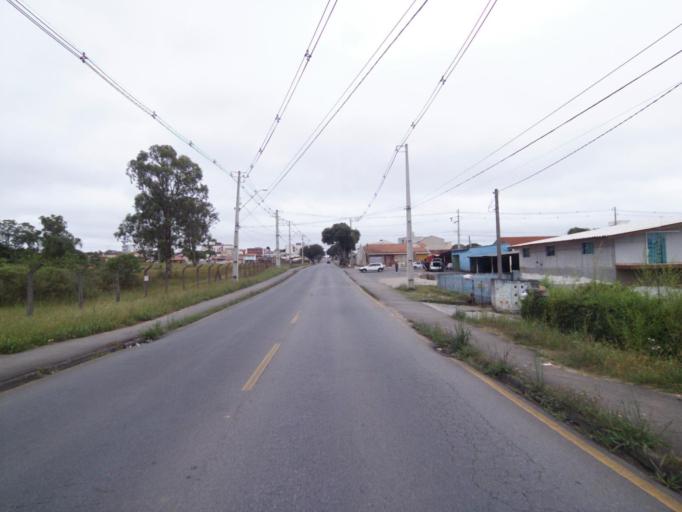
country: BR
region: Parana
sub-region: Sao Jose Dos Pinhais
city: Sao Jose dos Pinhais
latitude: -25.5385
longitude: -49.1823
